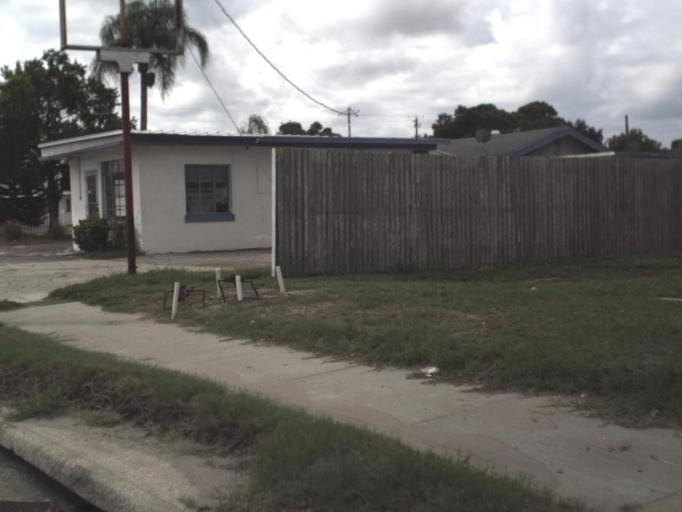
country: US
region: Florida
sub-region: Manatee County
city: Bayshore Gardens
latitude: 27.4282
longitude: -82.5756
